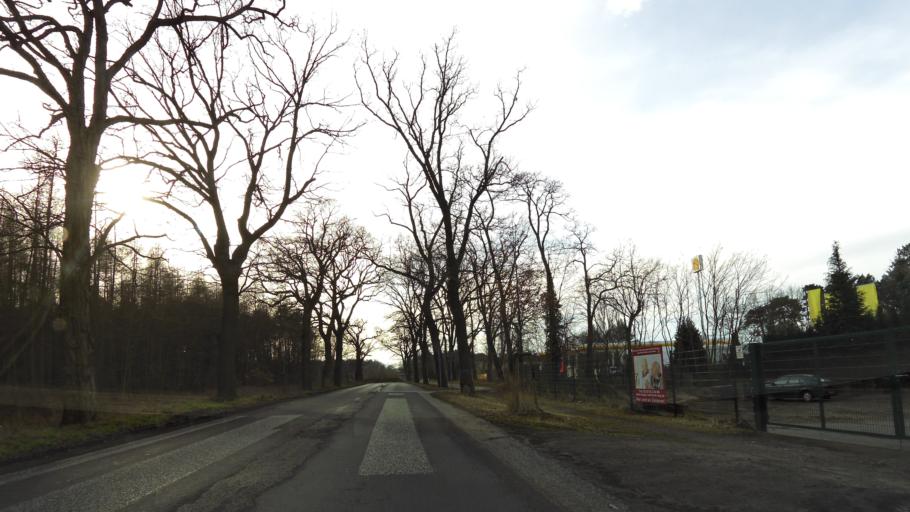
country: DE
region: Brandenburg
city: Michendorf
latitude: 52.3028
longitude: 13.0263
